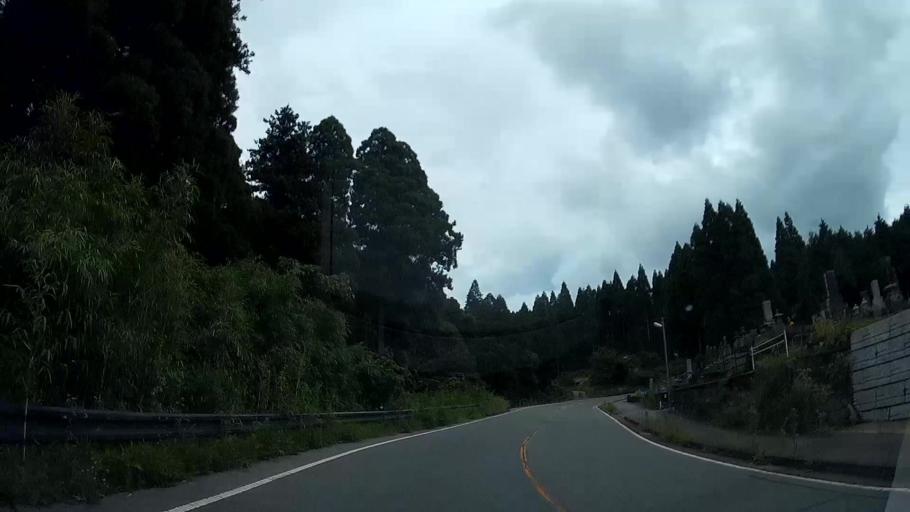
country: JP
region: Kumamoto
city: Aso
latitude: 32.9287
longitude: 131.0794
